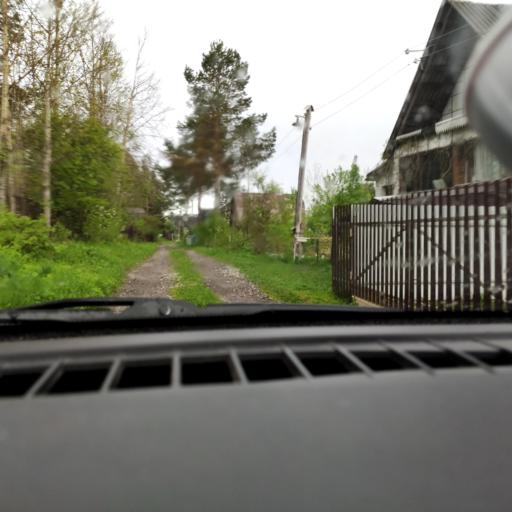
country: RU
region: Perm
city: Polazna
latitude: 58.2938
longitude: 56.1309
